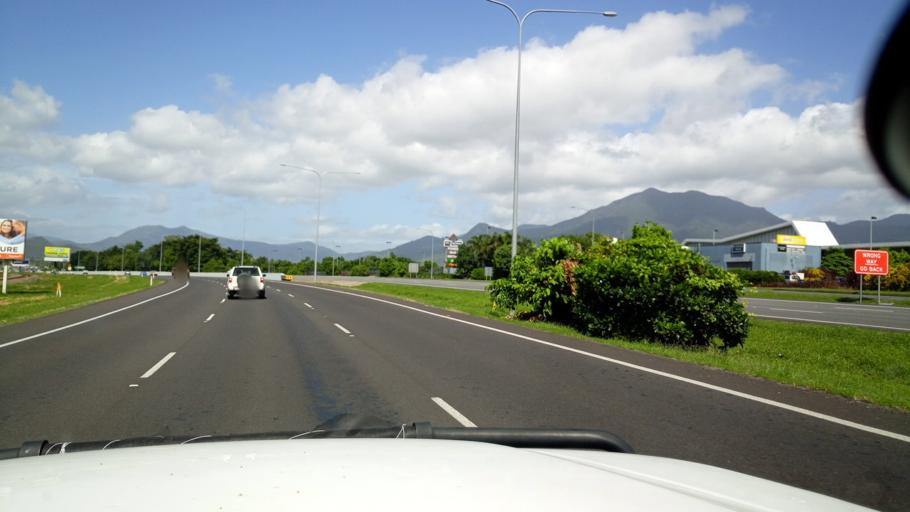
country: AU
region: Queensland
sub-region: Cairns
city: Woree
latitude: -16.9893
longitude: 145.7417
